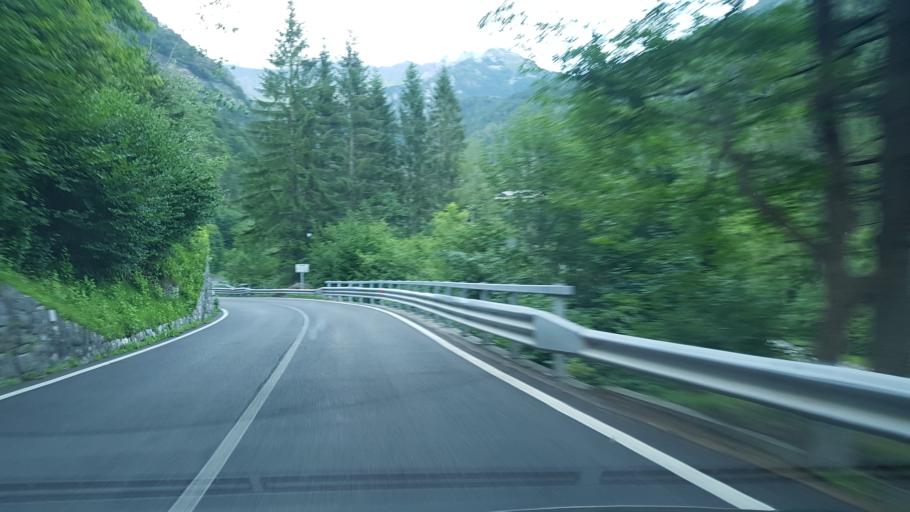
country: IT
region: Friuli Venezia Giulia
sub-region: Provincia di Udine
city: Forni Avoltri
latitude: 46.5888
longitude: 12.7733
